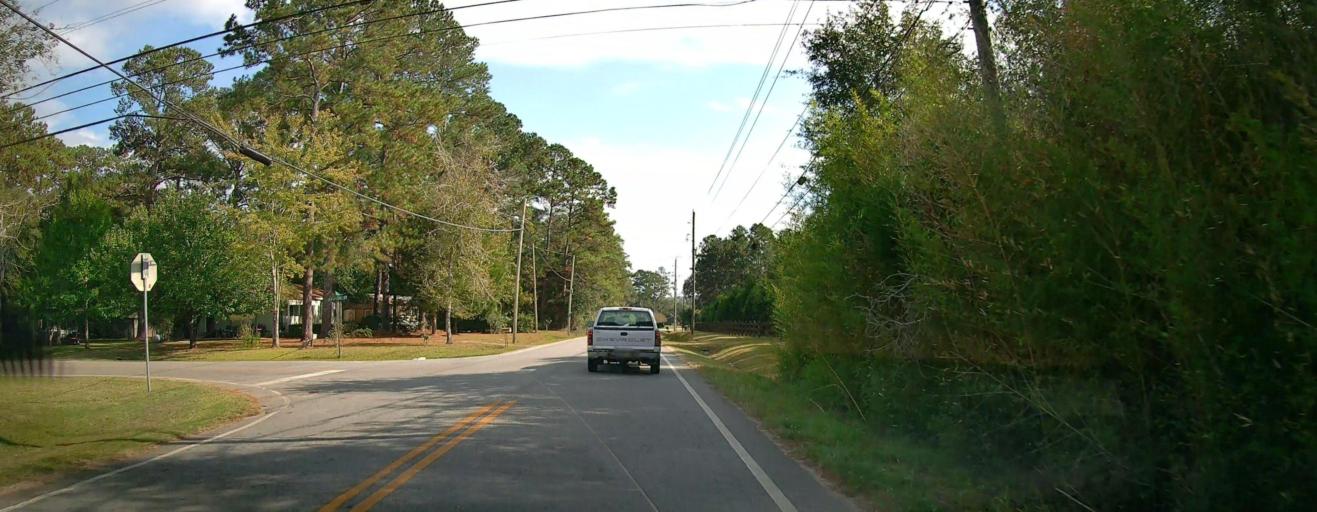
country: US
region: Georgia
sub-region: Thomas County
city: Thomasville
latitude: 30.8735
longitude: -84.0038
